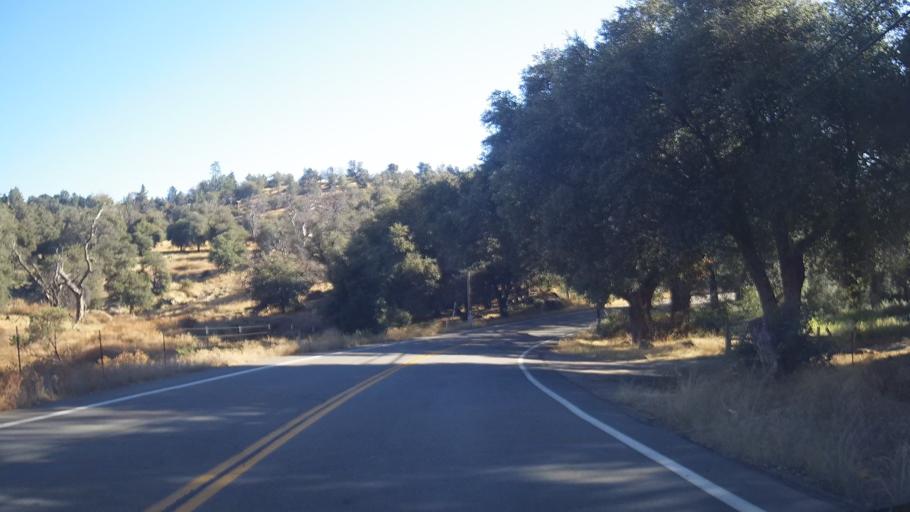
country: US
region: California
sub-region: San Diego County
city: Julian
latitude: 33.0612
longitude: -116.6179
